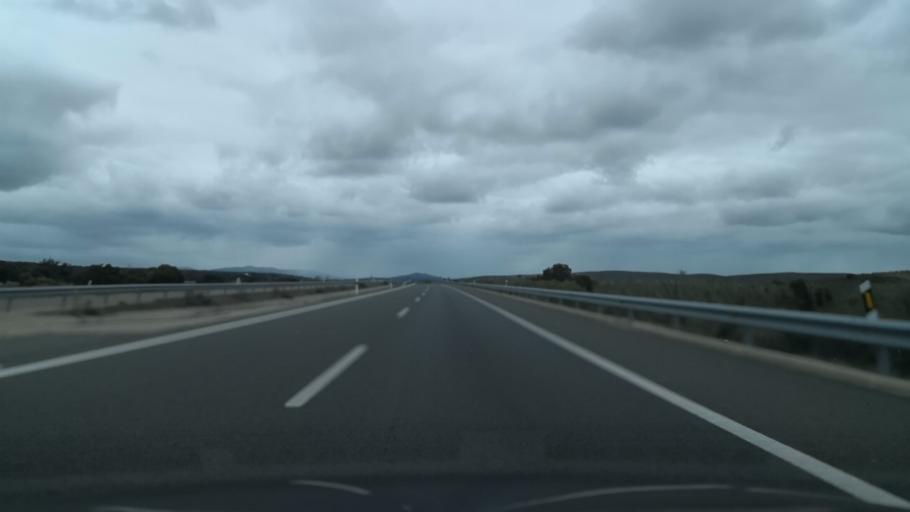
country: ES
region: Extremadura
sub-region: Provincia de Caceres
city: Galisteo
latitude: 39.9498
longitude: -6.1890
